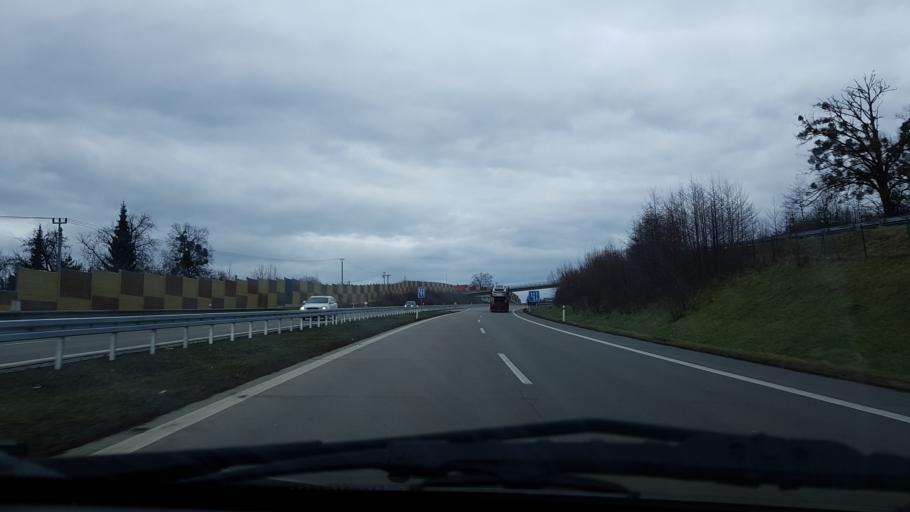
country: CZ
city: Komorni Lhotka
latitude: 49.7116
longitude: 18.5406
